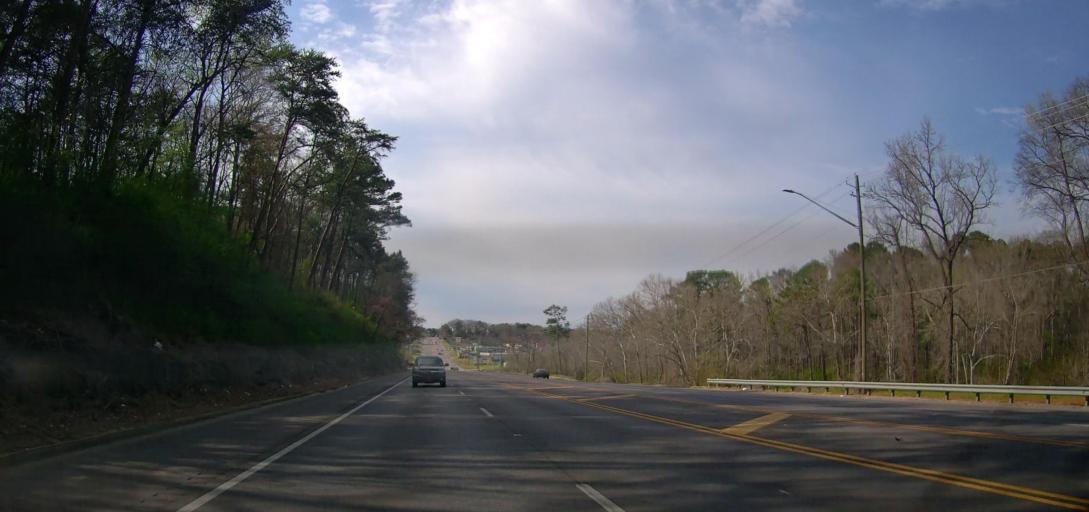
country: US
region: Alabama
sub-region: Jefferson County
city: Forestdale
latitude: 33.5495
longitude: -86.8812
